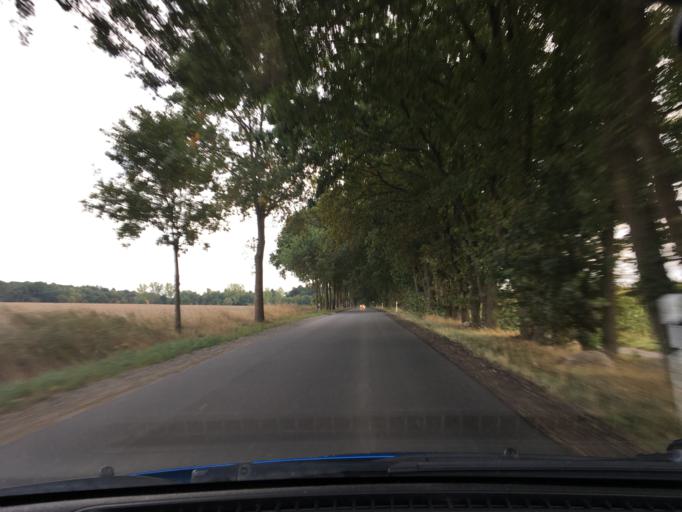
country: DE
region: Lower Saxony
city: Reppenstedt
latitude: 53.2421
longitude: 10.3666
